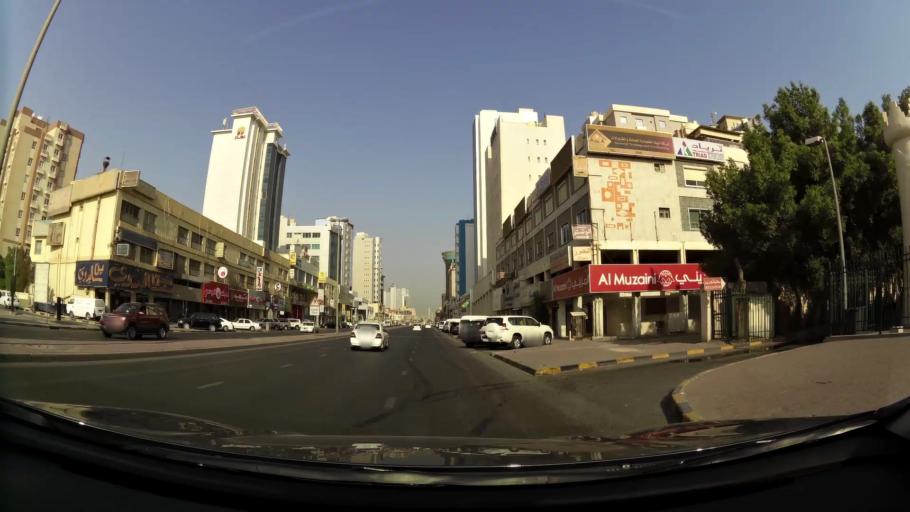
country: KW
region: Muhafazat Hawalli
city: Hawalli
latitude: 29.3407
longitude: 48.0205
